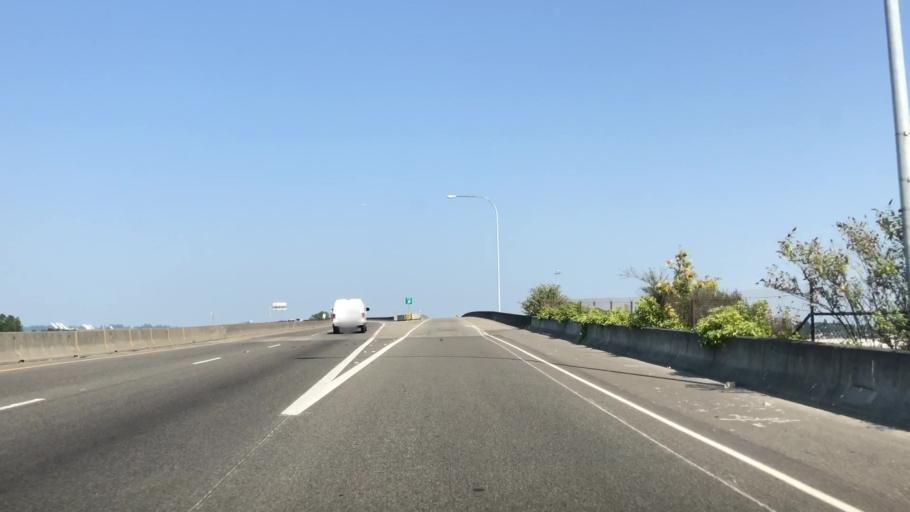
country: US
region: Washington
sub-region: Pierce County
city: Tacoma
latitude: 47.2443
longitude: -122.4189
